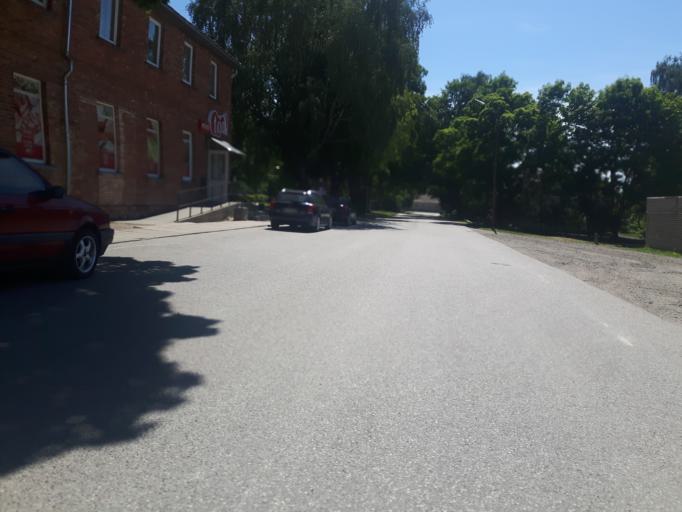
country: LV
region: Grobina
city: Grobina
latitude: 56.5323
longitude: 21.1567
